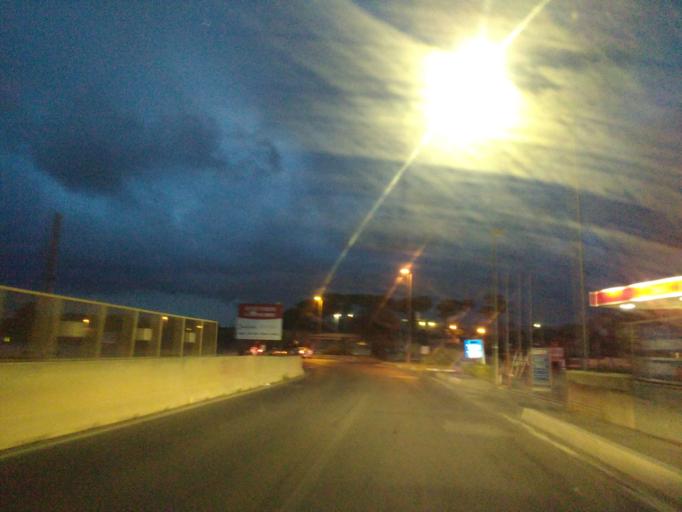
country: IT
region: Latium
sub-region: Citta metropolitana di Roma Capitale
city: Anzio
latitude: 41.4536
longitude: 12.6225
